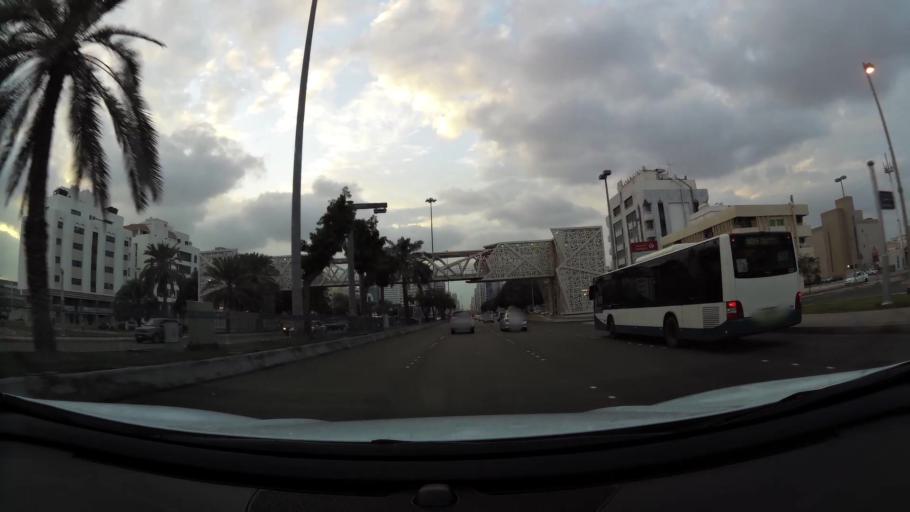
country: AE
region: Abu Dhabi
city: Abu Dhabi
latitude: 24.4550
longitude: 54.3852
